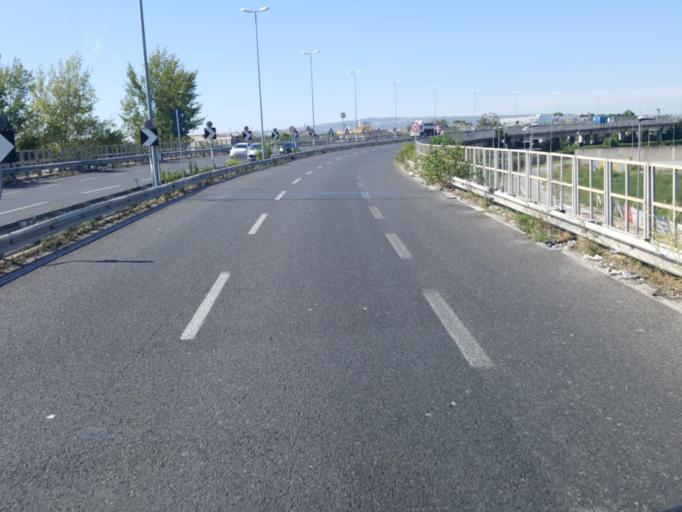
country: IT
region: Campania
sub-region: Provincia di Napoli
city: Frattamaggiore
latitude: 40.9289
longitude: 14.2810
